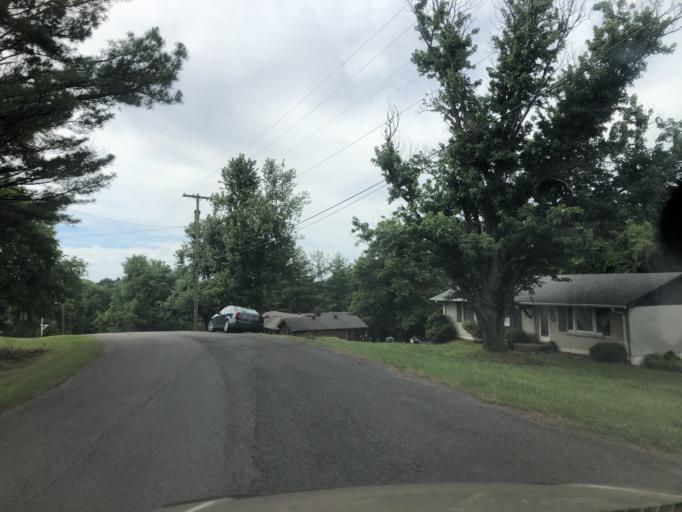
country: US
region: Tennessee
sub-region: Davidson County
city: Lakewood
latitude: 36.2605
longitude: -86.6162
